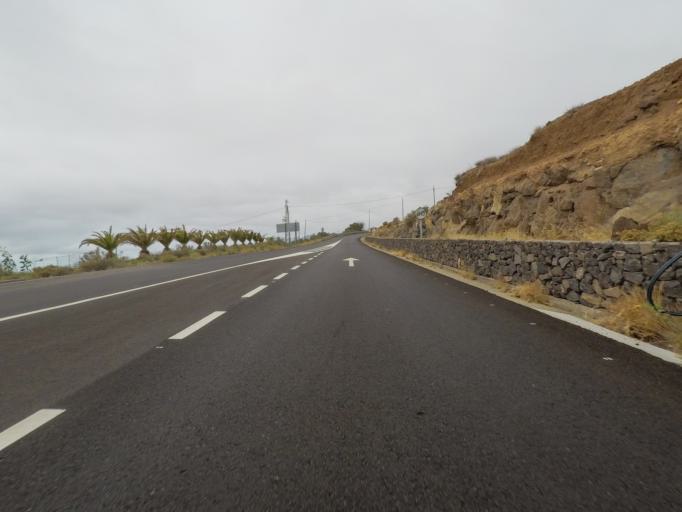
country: ES
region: Canary Islands
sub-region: Provincia de Santa Cruz de Tenerife
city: Alajero
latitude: 28.0449
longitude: -17.1964
